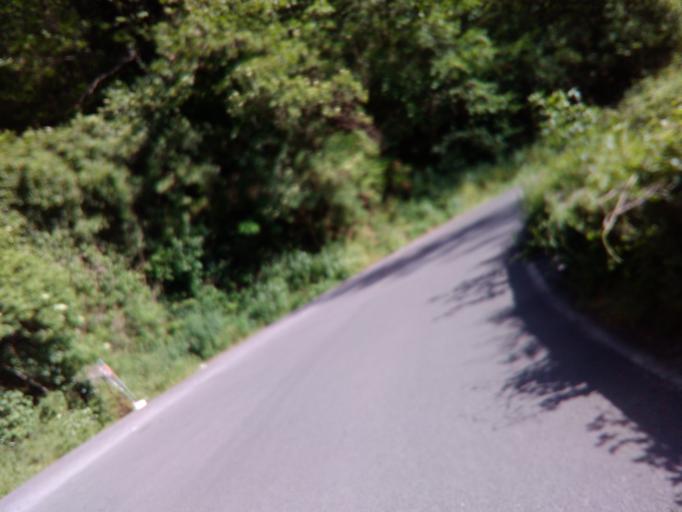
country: IT
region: Tuscany
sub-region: Provincia di Massa-Carrara
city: Fosdinovo
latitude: 44.1206
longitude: 10.0659
